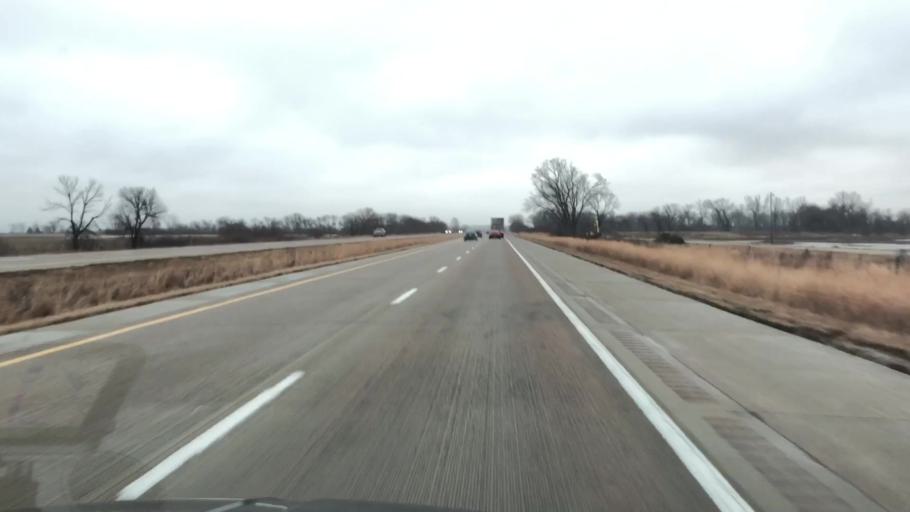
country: US
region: Nebraska
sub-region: Burt County
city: Tekamah
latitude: 41.8468
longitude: -96.0955
